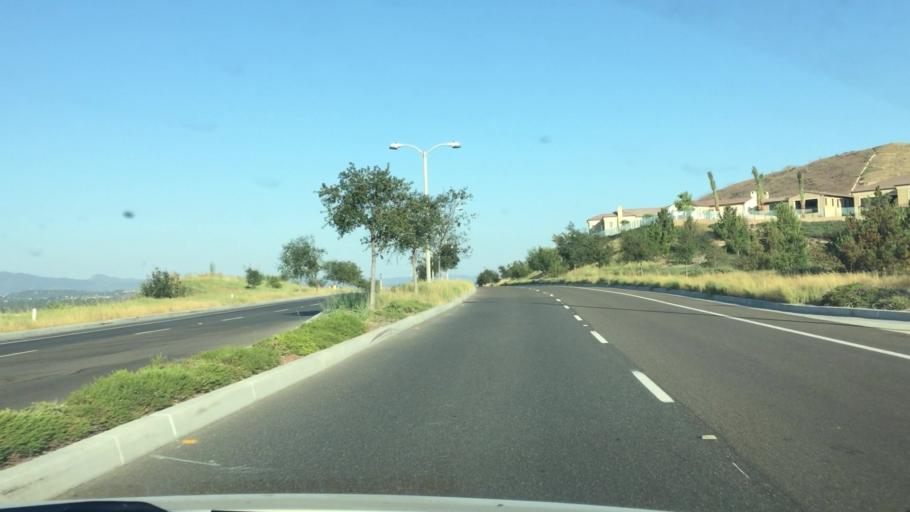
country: US
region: California
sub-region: Orange County
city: Laguna Woods
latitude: 33.6366
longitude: -117.7554
